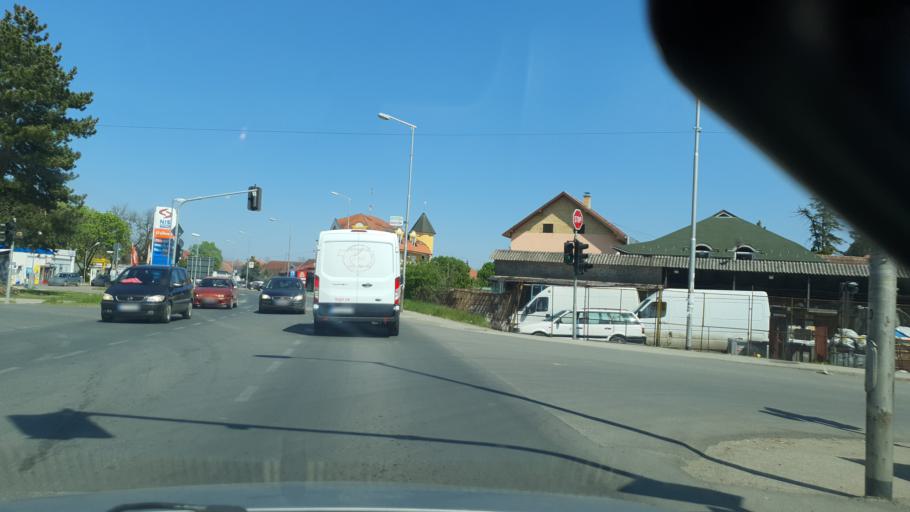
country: RS
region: Autonomna Pokrajina Vojvodina
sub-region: Juznobacki Okrug
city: Beocin
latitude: 45.2386
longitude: 19.7010
